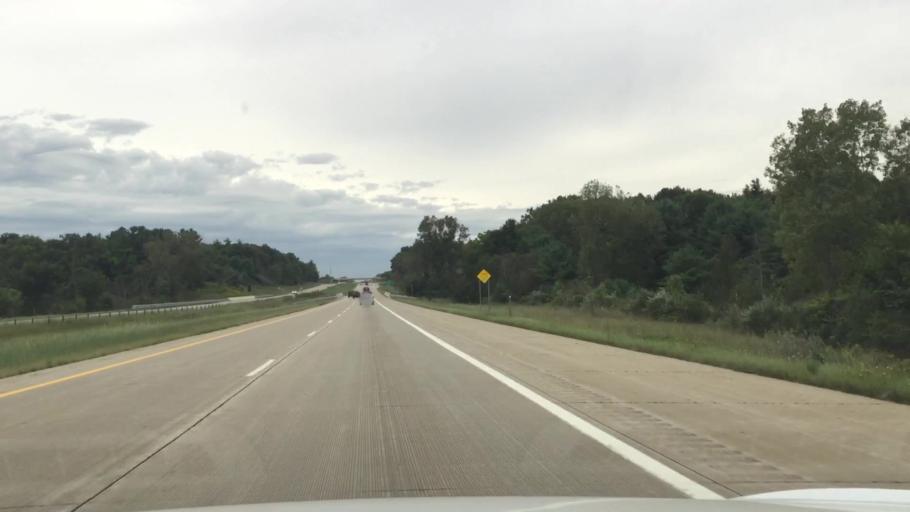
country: US
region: Michigan
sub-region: Saint Clair County
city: Marysville
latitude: 42.8712
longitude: -82.5453
